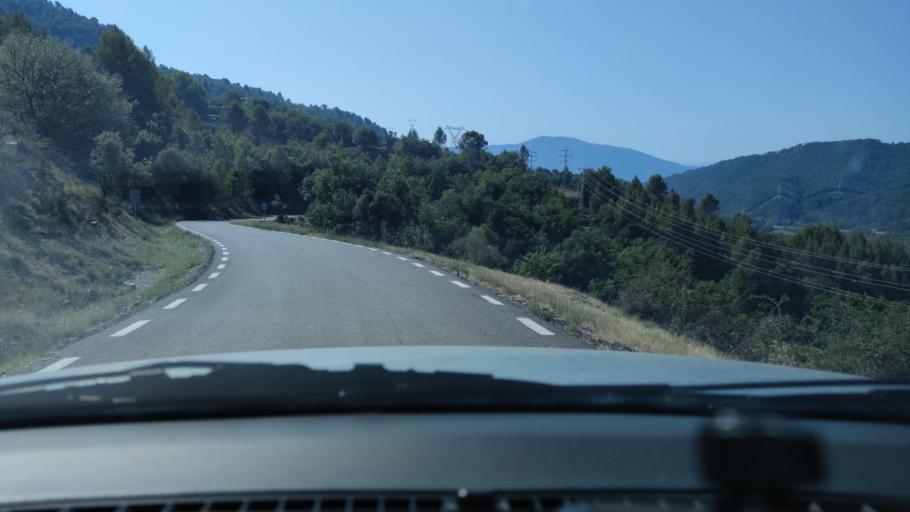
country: ES
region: Catalonia
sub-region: Provincia de Lleida
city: Senterada
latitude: 42.2734
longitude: 0.9507
